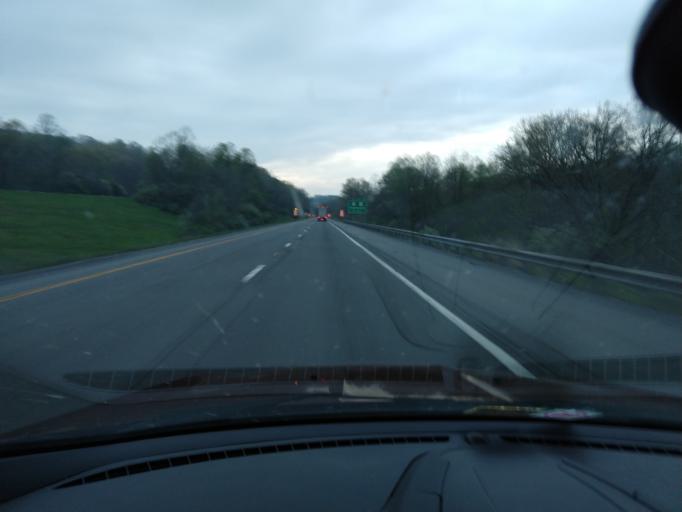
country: US
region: West Virginia
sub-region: Braxton County
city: Sutton
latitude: 38.6886
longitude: -80.6908
